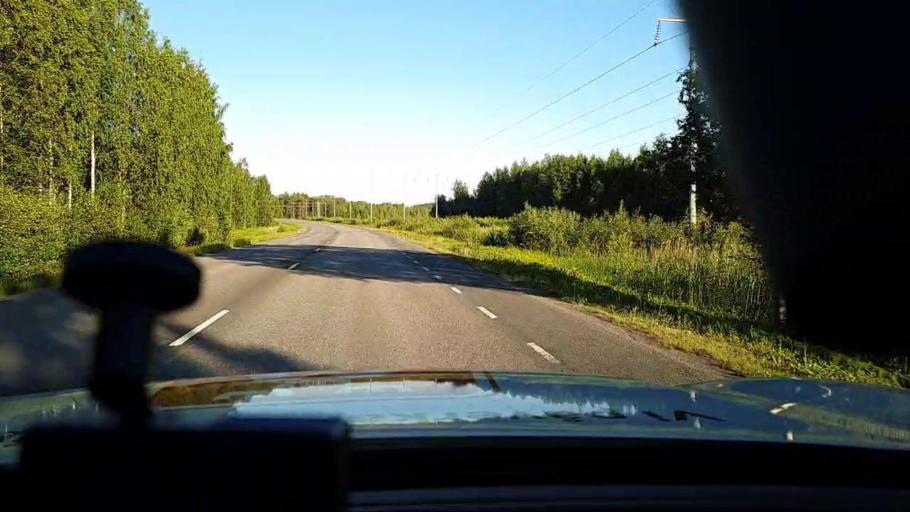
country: SE
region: Norrbotten
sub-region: Lulea Kommun
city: Lulea
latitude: 65.6099
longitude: 22.1656
